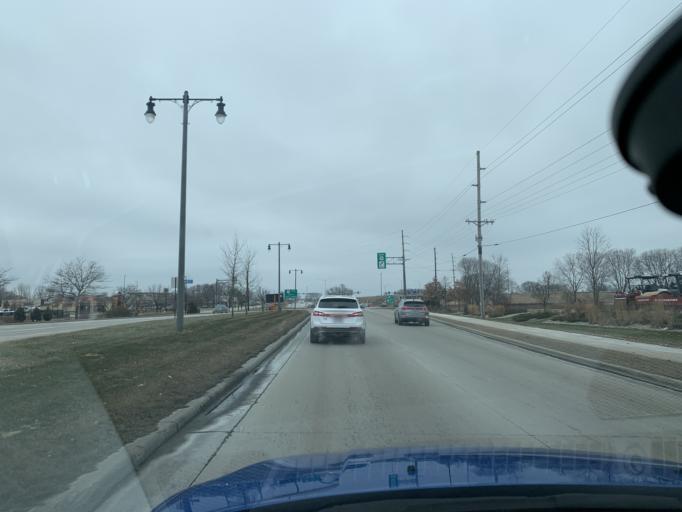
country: US
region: Wisconsin
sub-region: Dane County
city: Sun Prairie
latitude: 43.1767
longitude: -89.2457
